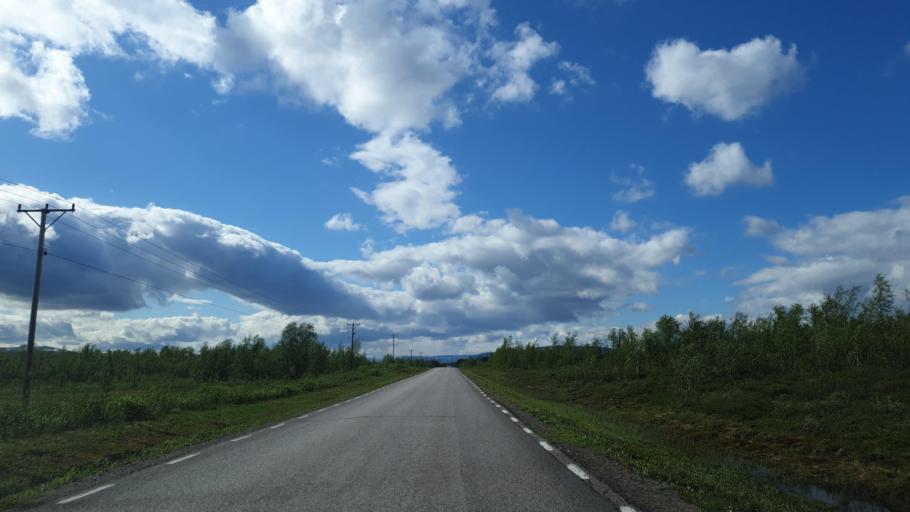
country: SE
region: Norrbotten
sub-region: Kiruna Kommun
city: Kiruna
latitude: 67.7621
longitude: 20.0033
